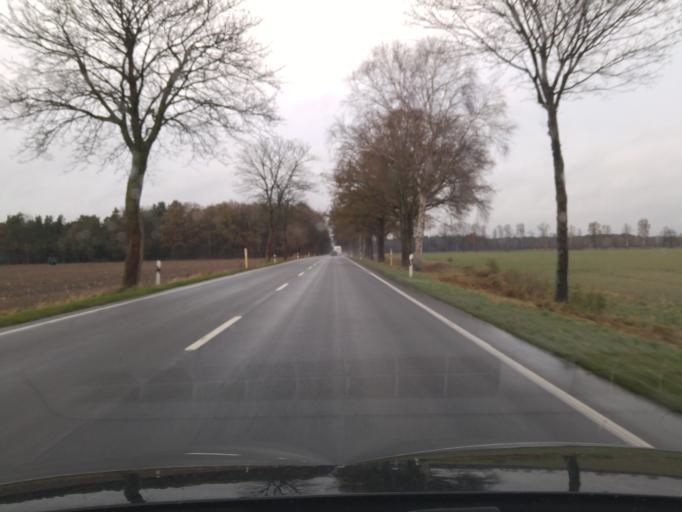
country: DE
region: Lower Saxony
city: Gross Oesingen
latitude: 52.6701
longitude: 10.4682
